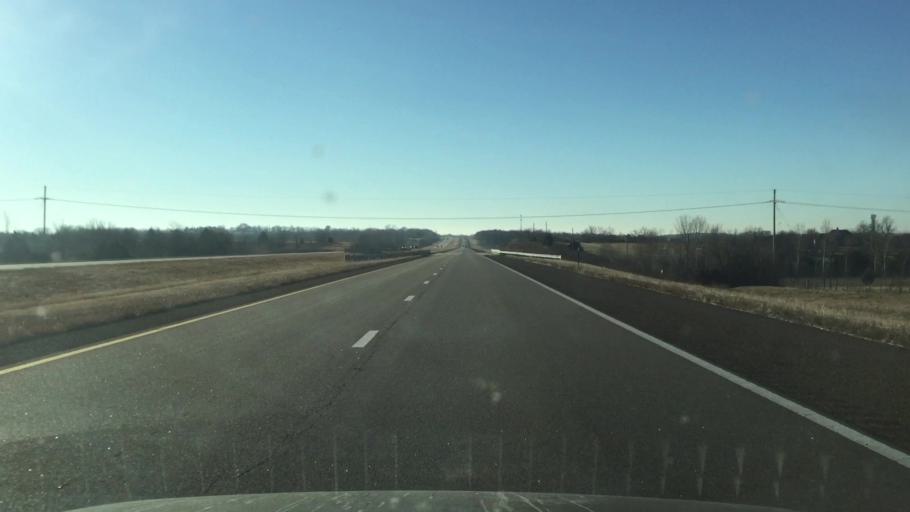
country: US
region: Kansas
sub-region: Miami County
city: Paola
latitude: 38.6083
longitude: -94.8356
